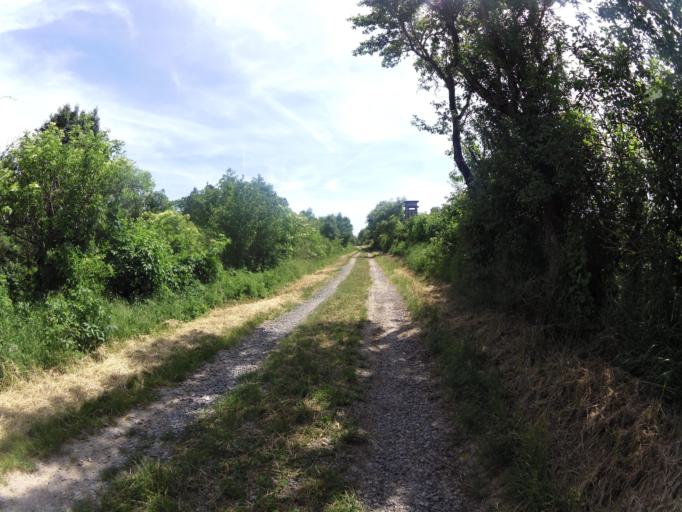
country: DE
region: Bavaria
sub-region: Regierungsbezirk Unterfranken
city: Sommerhausen
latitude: 49.6740
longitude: 10.0288
